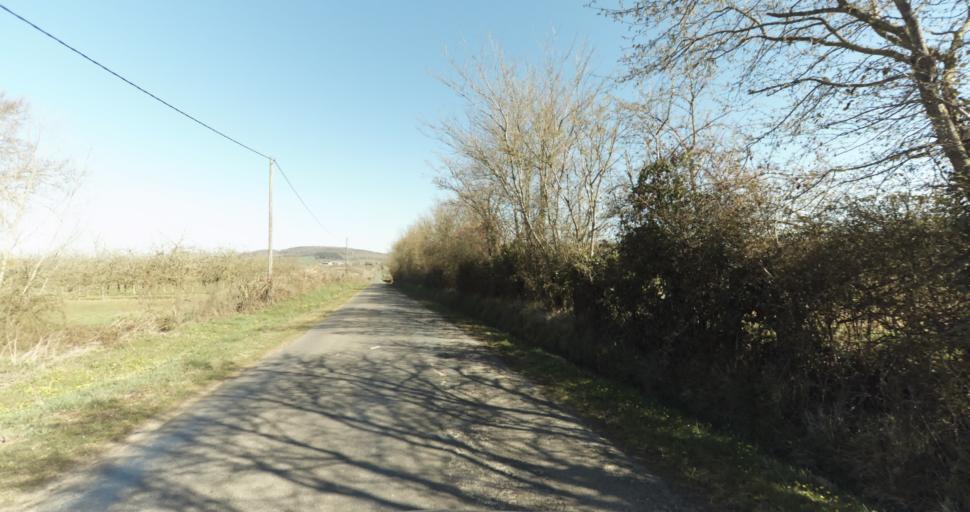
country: FR
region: Lower Normandy
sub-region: Departement du Calvados
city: Saint-Pierre-sur-Dives
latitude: 48.9527
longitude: 0.0488
